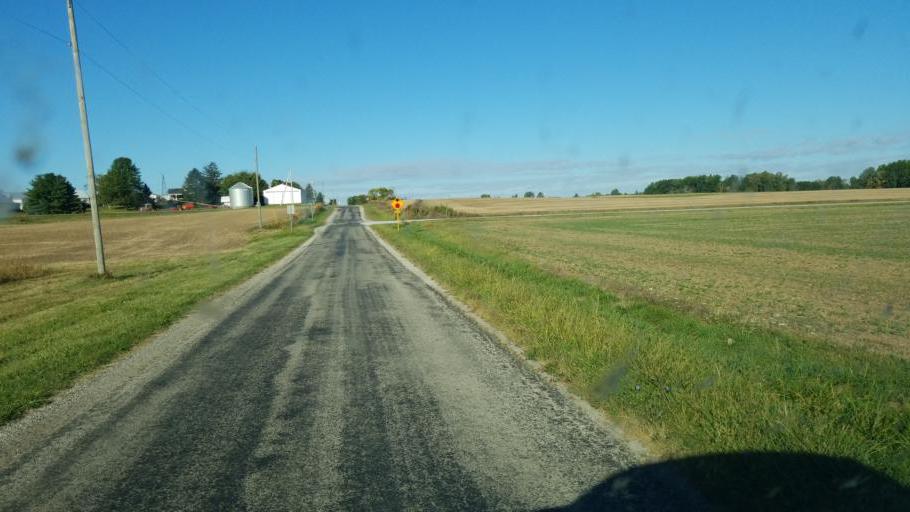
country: US
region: Ohio
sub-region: Crawford County
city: Galion
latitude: 40.6977
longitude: -82.8642
